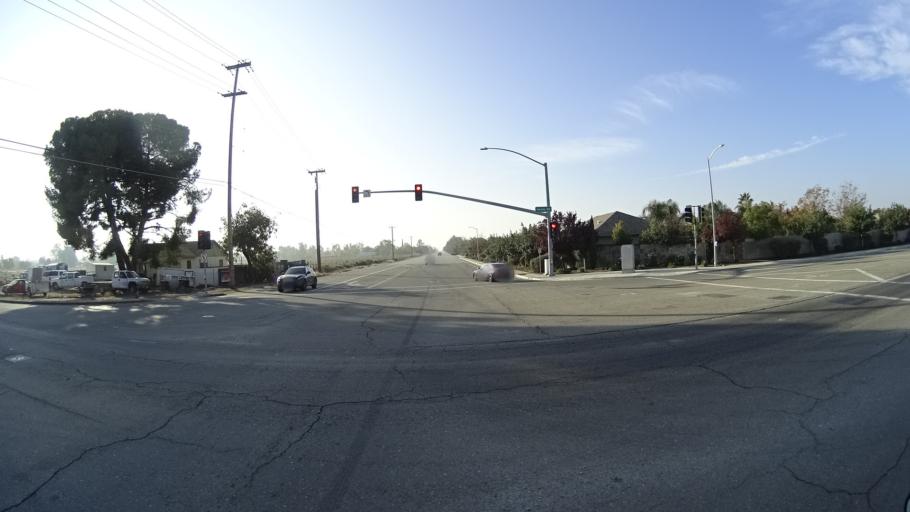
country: US
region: California
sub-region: Kern County
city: Rosedale
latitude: 35.3835
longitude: -119.1635
